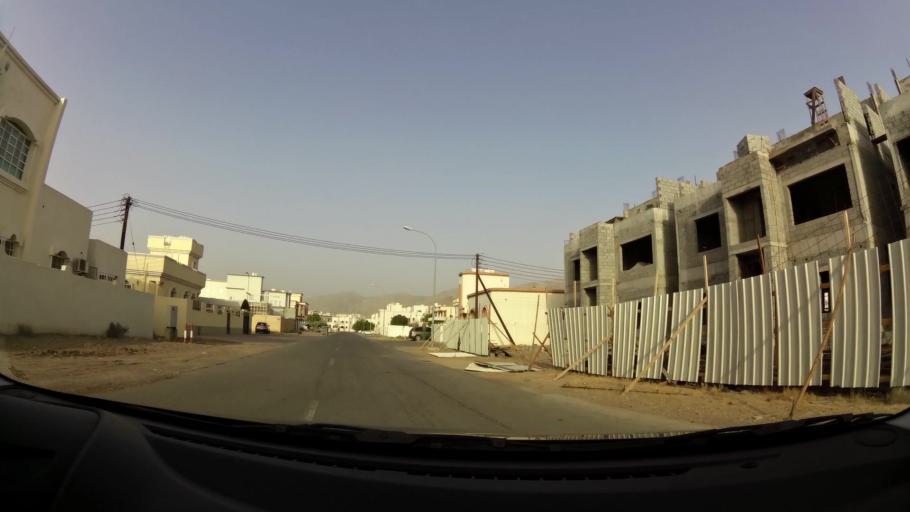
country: OM
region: Muhafazat Masqat
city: Bawshar
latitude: 23.5321
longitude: 58.3503
